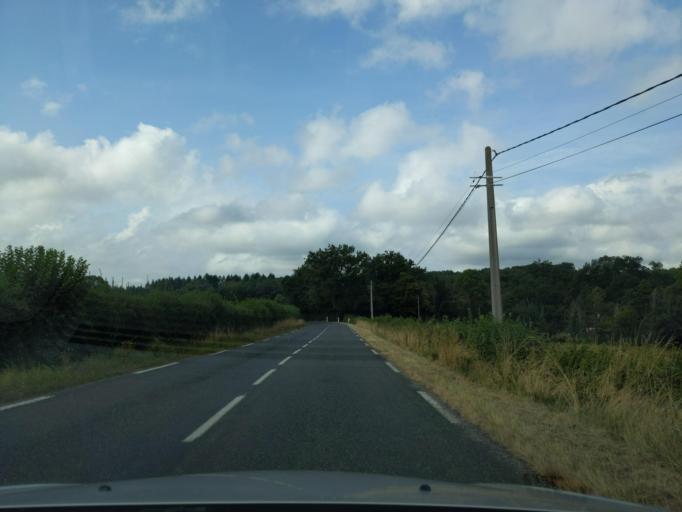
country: FR
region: Bourgogne
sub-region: Departement de la Nievre
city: Luzy
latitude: 46.7201
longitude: 3.8836
